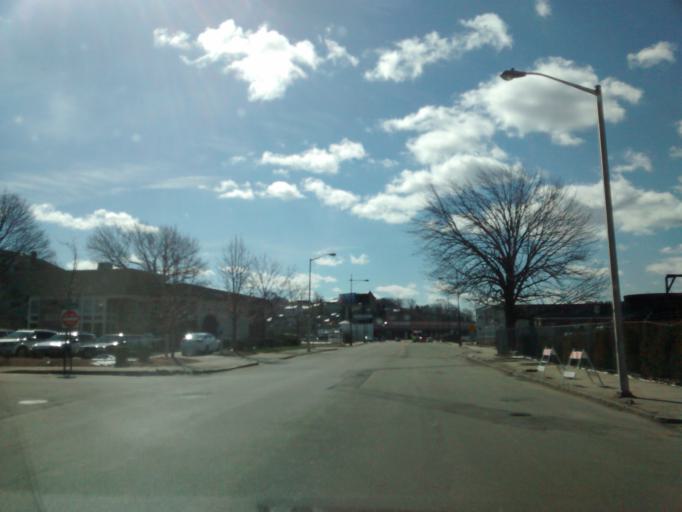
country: US
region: Massachusetts
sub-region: Worcester County
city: Worcester
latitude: 42.2489
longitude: -71.8043
